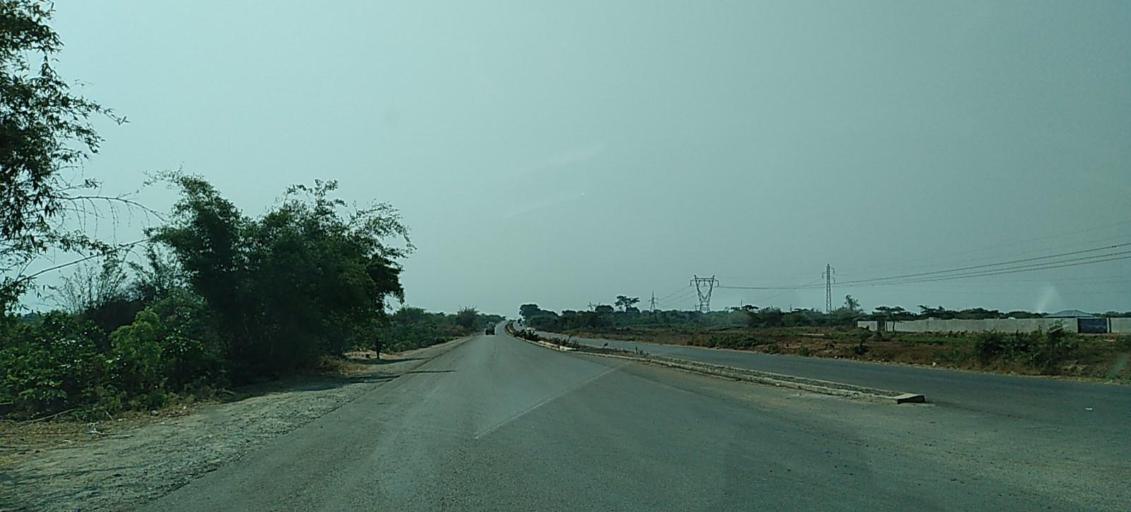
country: ZM
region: Copperbelt
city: Chingola
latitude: -12.5756
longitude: 27.9182
